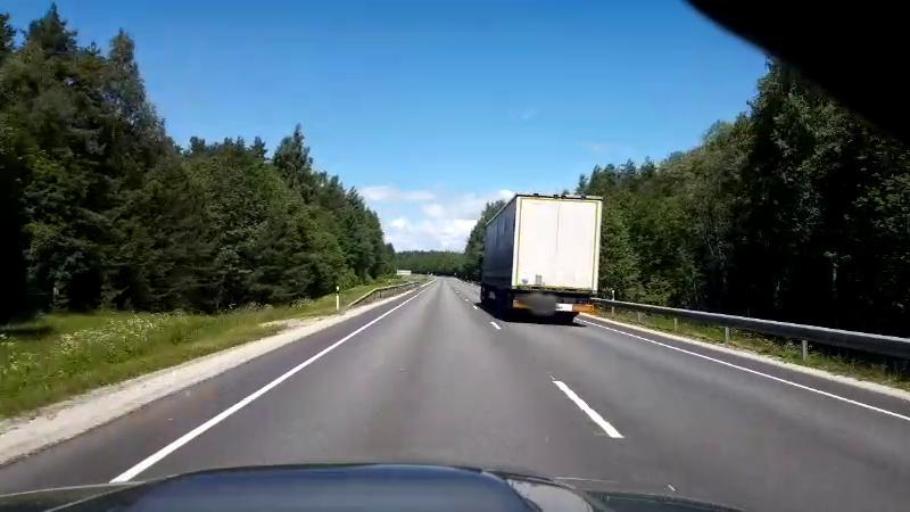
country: EE
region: Paernumaa
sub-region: Paernu linn
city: Parnu
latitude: 58.1301
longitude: 24.5128
